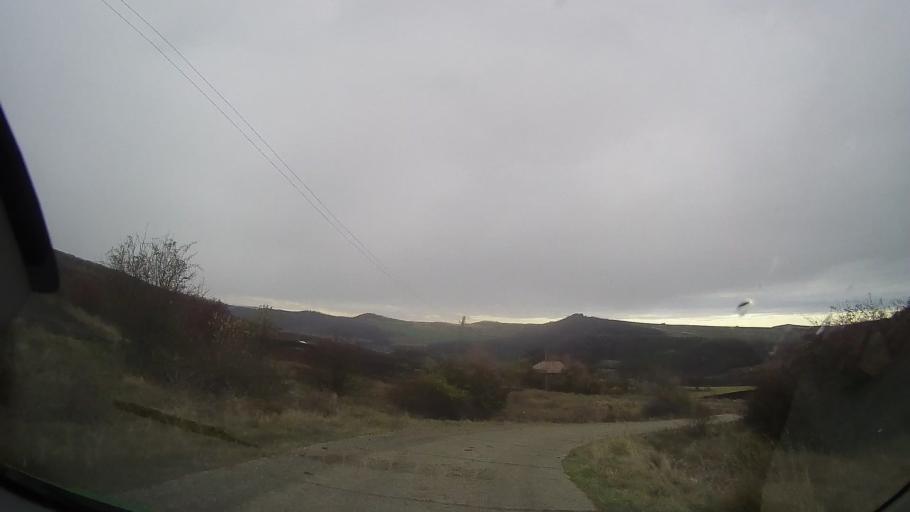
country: RO
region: Mures
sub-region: Comuna Bala
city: Bala
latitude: 46.6757
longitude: 24.4837
